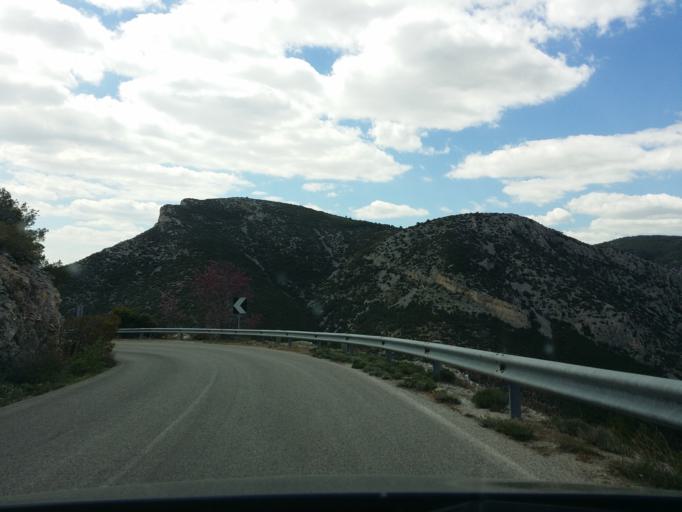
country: GR
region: Attica
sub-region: Nomarchia Dytikis Attikis
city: Fyli
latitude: 38.1157
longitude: 23.6465
